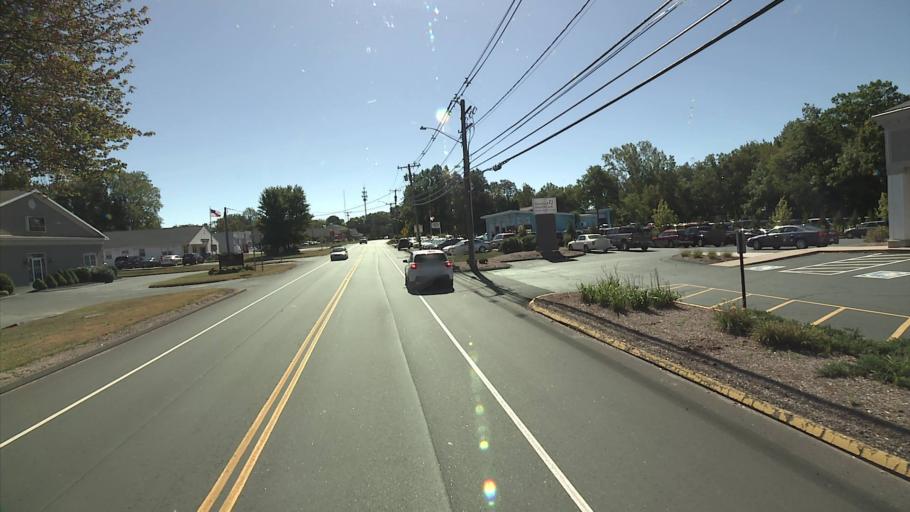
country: US
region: Connecticut
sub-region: New Haven County
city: Prospect
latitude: 41.5142
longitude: -72.9856
